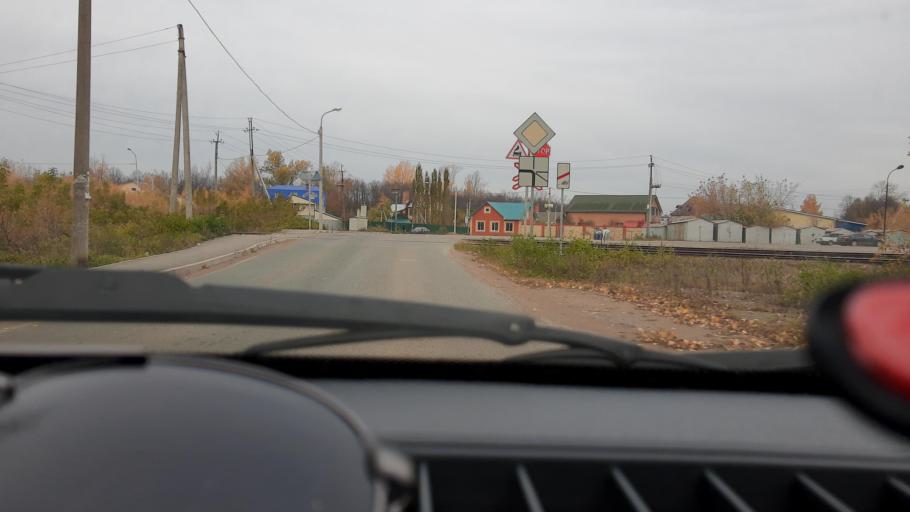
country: RU
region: Bashkortostan
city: Ufa
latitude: 54.6670
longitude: 55.9422
